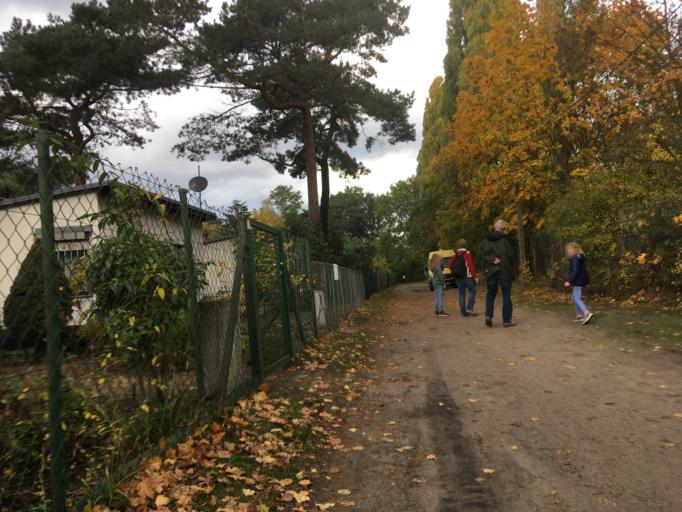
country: DE
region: Berlin
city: Adlershof
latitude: 52.4518
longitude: 13.5556
